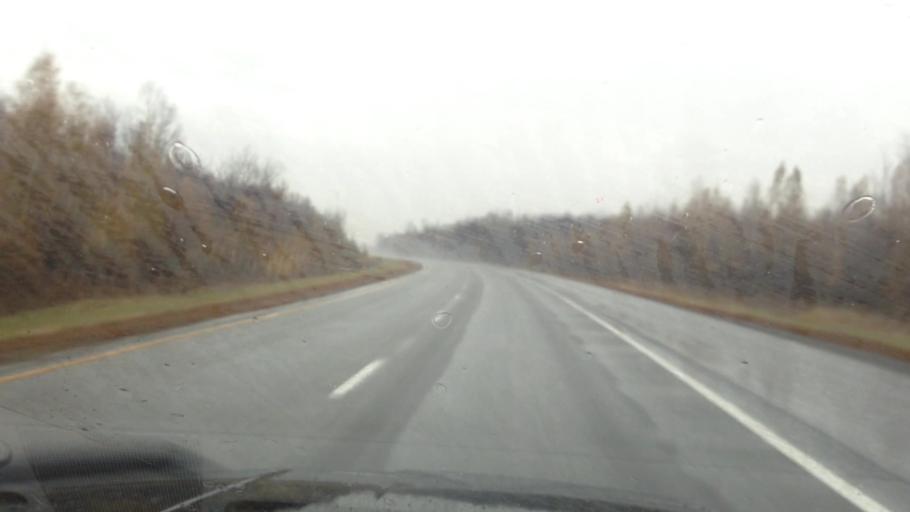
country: CA
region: Ontario
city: Casselman
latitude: 45.3050
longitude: -75.1444
